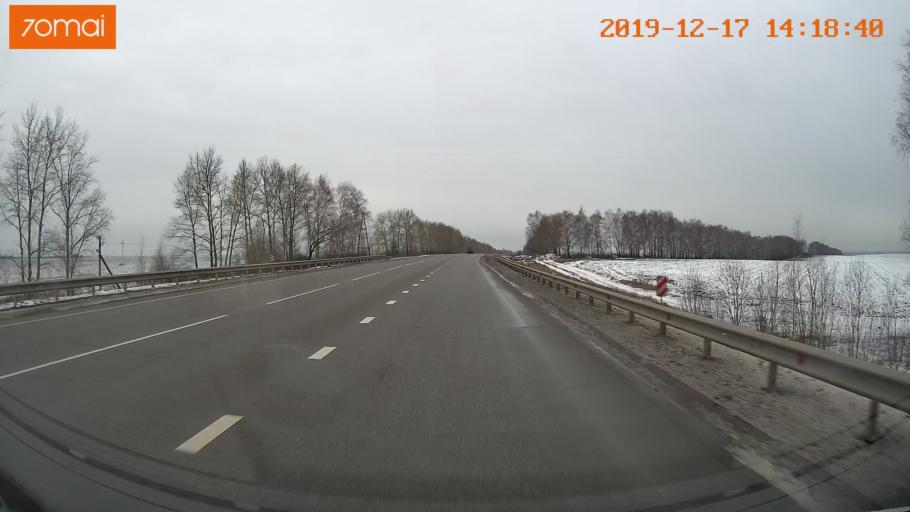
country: RU
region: Rjazan
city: Zakharovo
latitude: 54.4563
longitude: 39.4402
